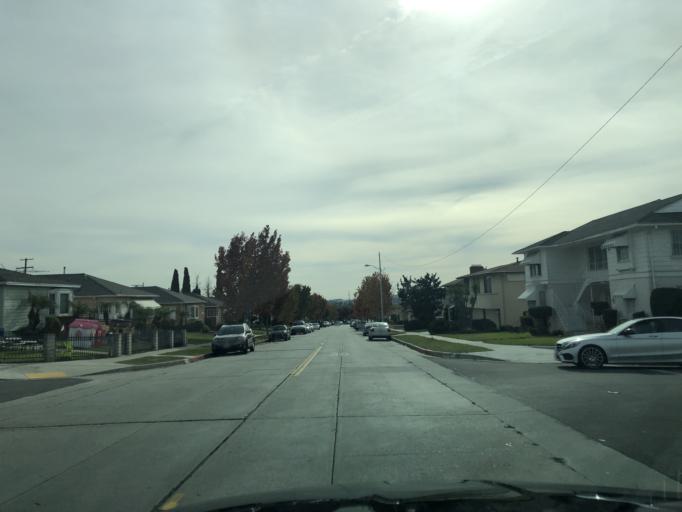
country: US
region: California
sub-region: Los Angeles County
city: Ladera Heights
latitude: 33.9868
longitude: -118.3625
